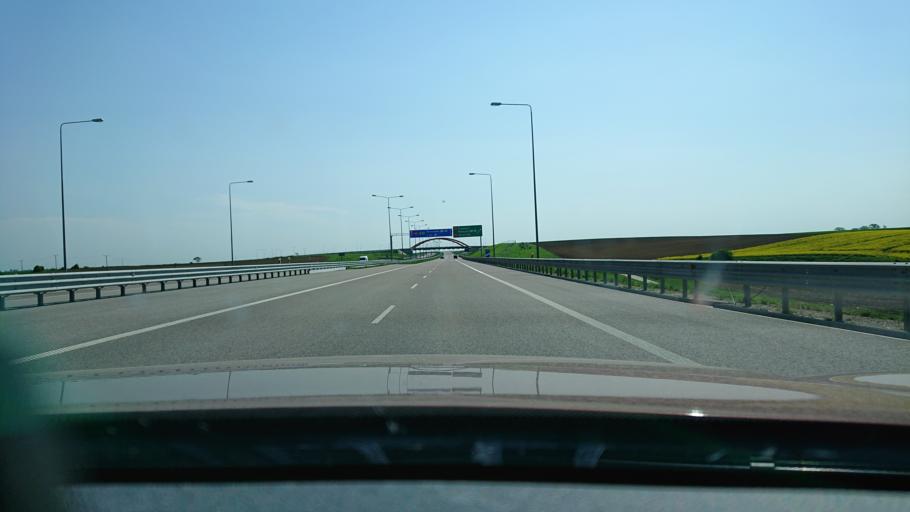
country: PL
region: Subcarpathian Voivodeship
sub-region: Powiat jaroslawski
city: Radymno
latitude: 49.9130
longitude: 22.8004
